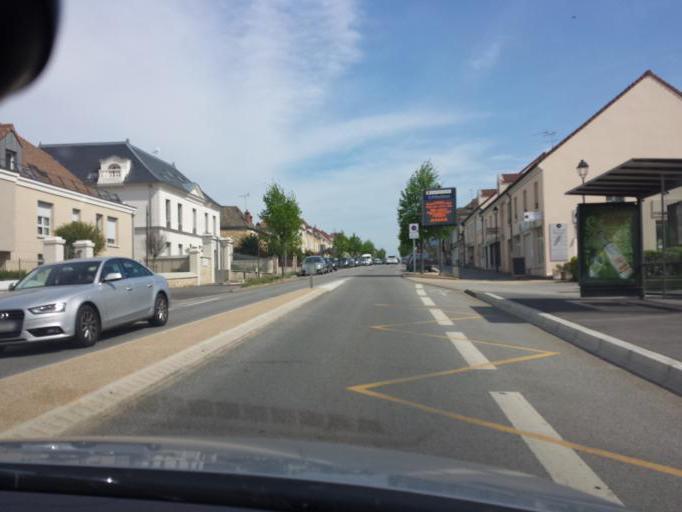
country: FR
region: Ile-de-France
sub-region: Departement des Yvelines
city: Neauphle-le-Chateau
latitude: 48.8039
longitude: 1.8969
